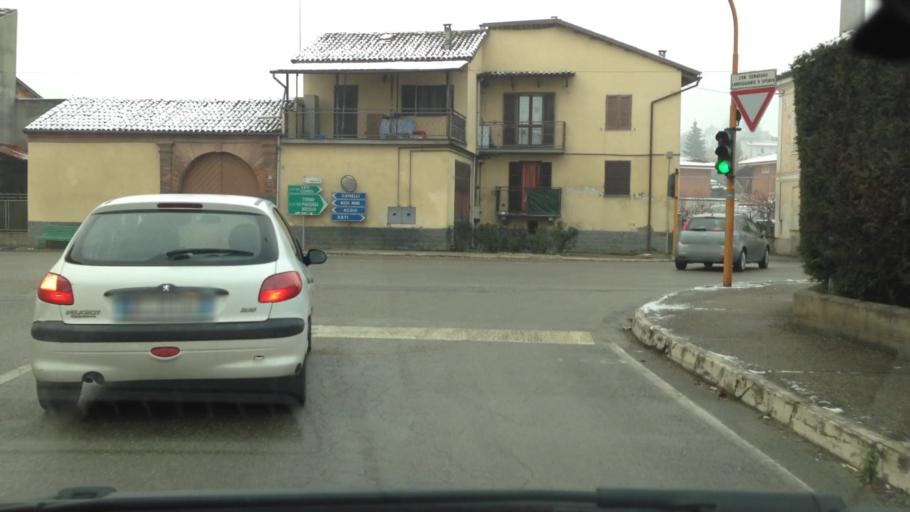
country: IT
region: Piedmont
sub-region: Provincia di Asti
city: Montegrosso
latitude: 44.8190
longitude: 8.2352
